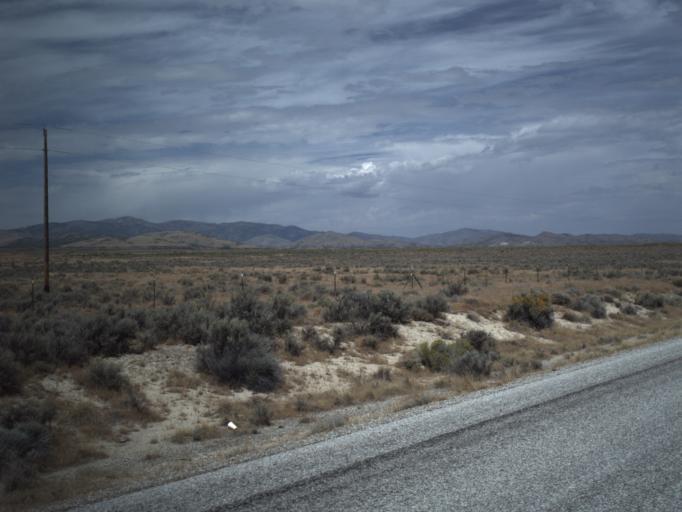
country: US
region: Utah
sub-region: Tooele County
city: Wendover
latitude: 41.5334
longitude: -113.5928
